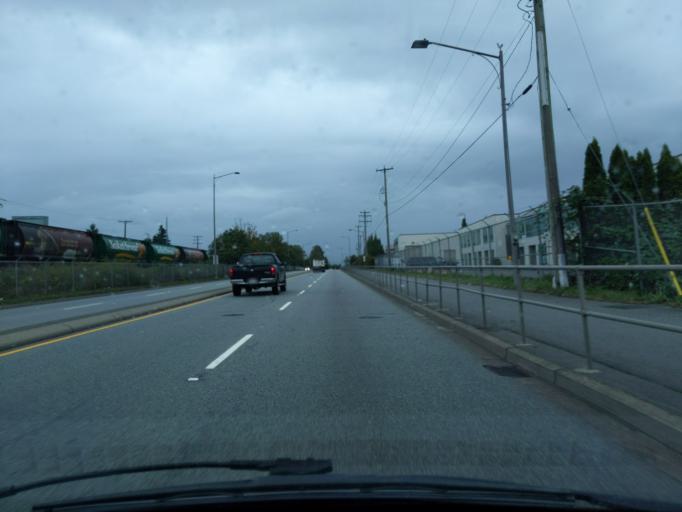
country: CA
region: British Columbia
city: Pitt Meadows
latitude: 49.1806
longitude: -122.7037
